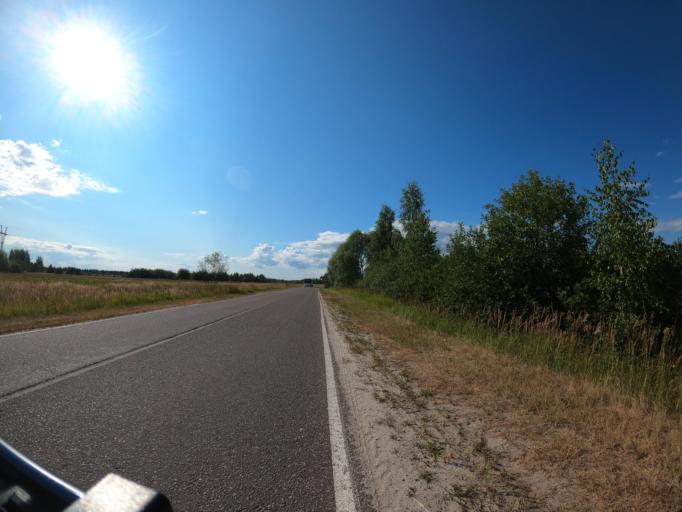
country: RU
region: Moskovskaya
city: Konobeyevo
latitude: 55.3982
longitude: 38.7152
